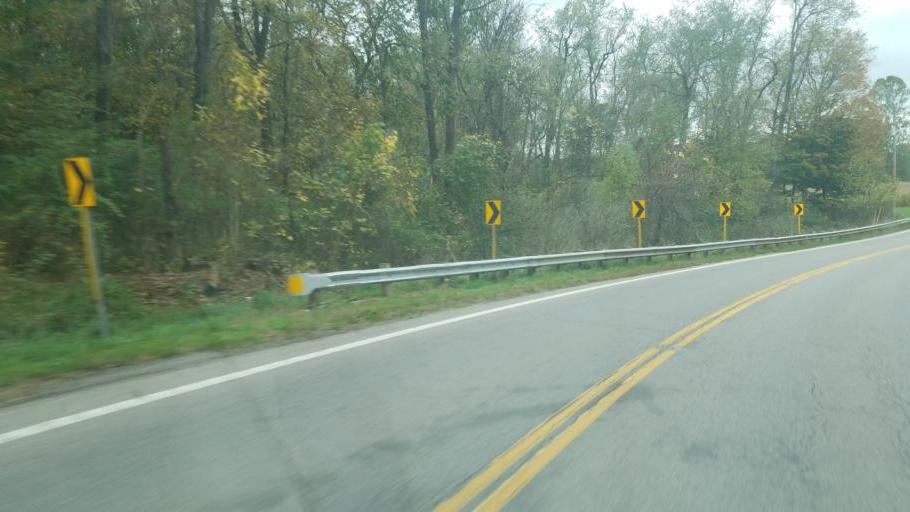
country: US
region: Ohio
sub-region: Richland County
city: Lincoln Heights
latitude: 40.7047
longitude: -82.4065
